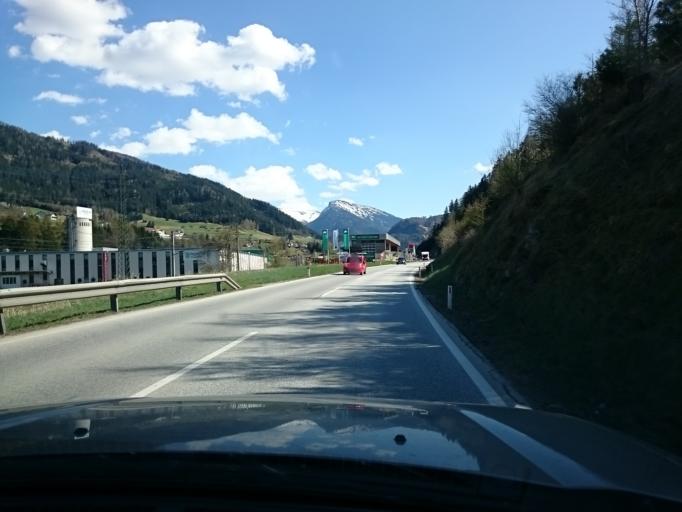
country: AT
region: Tyrol
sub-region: Politischer Bezirk Innsbruck Land
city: Steinach am Brenner
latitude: 47.1019
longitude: 11.4624
